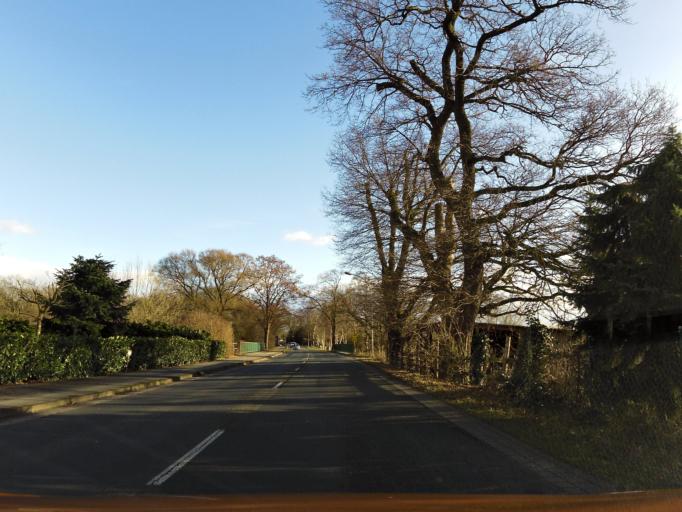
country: DE
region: Lower Saxony
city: Verden
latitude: 52.9054
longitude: 9.2742
